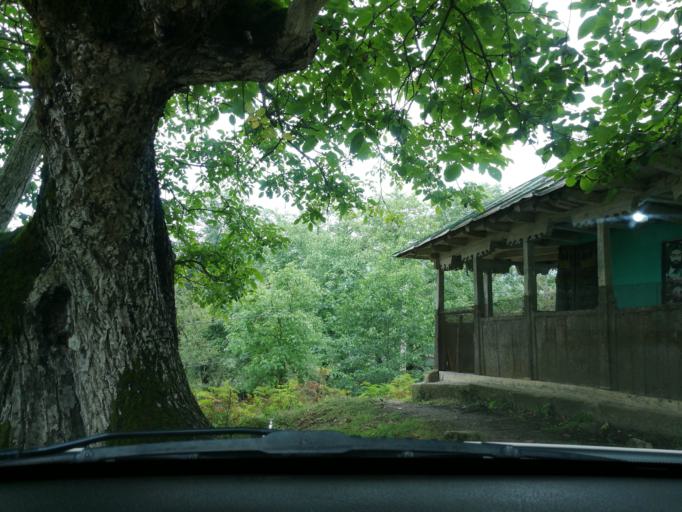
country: IR
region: Mazandaran
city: `Abbasabad
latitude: 36.4937
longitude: 51.2075
